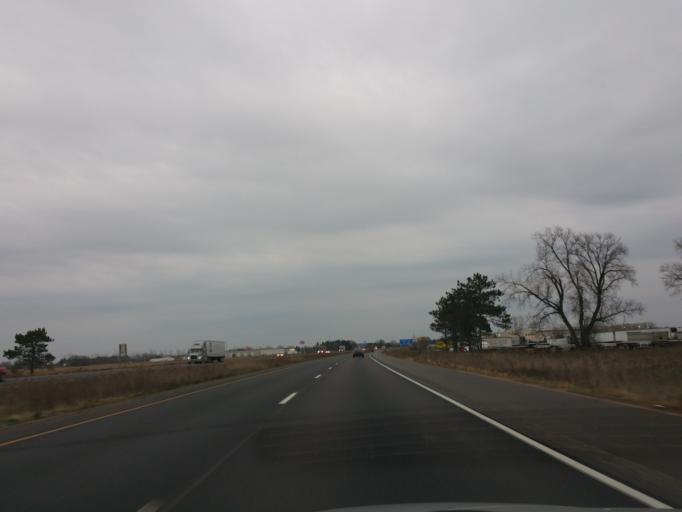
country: US
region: Wisconsin
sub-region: Eau Claire County
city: Eau Claire
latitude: 44.8470
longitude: -91.6189
